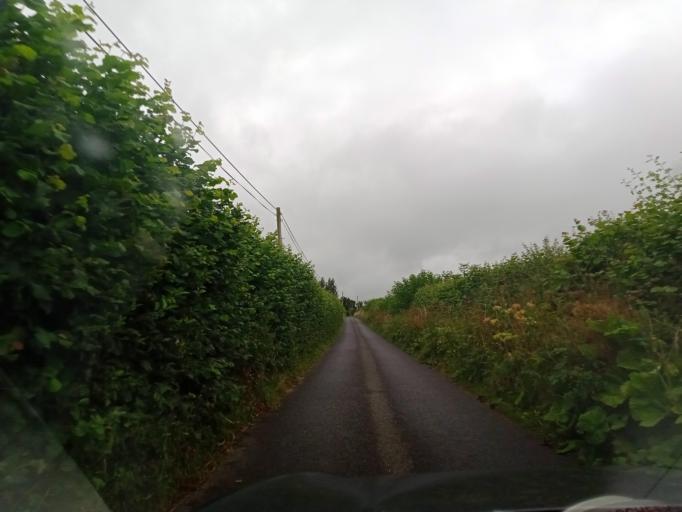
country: IE
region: Leinster
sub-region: Laois
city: Stradbally
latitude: 52.9522
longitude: -7.2247
